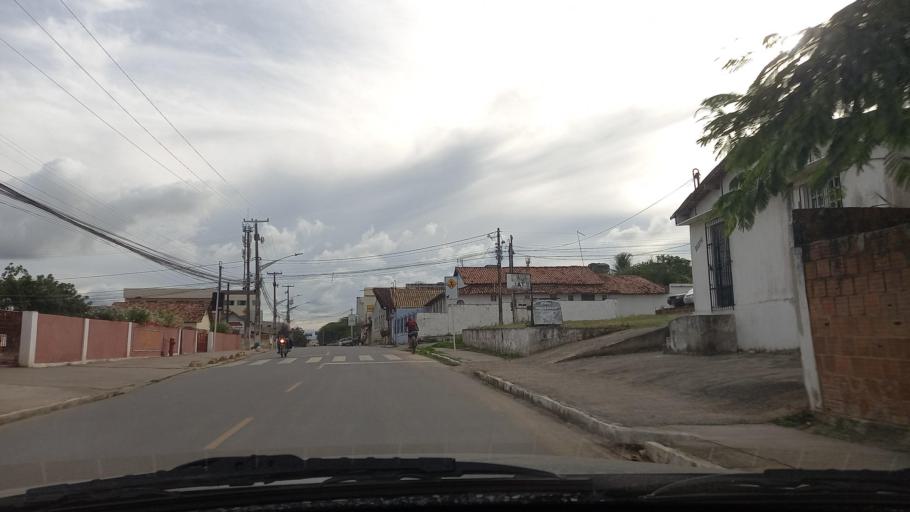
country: BR
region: Pernambuco
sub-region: Gravata
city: Gravata
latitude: -8.1951
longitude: -35.5505
